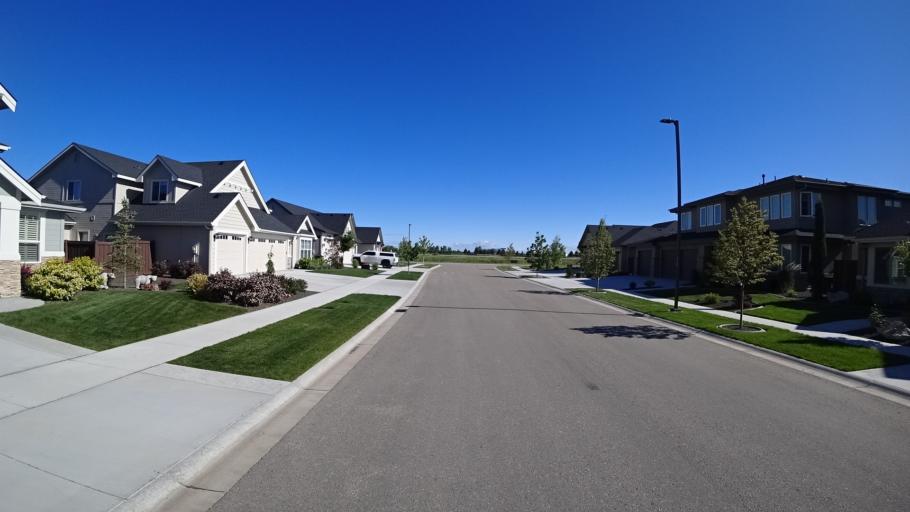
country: US
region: Idaho
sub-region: Ada County
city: Star
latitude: 43.6589
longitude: -116.4420
